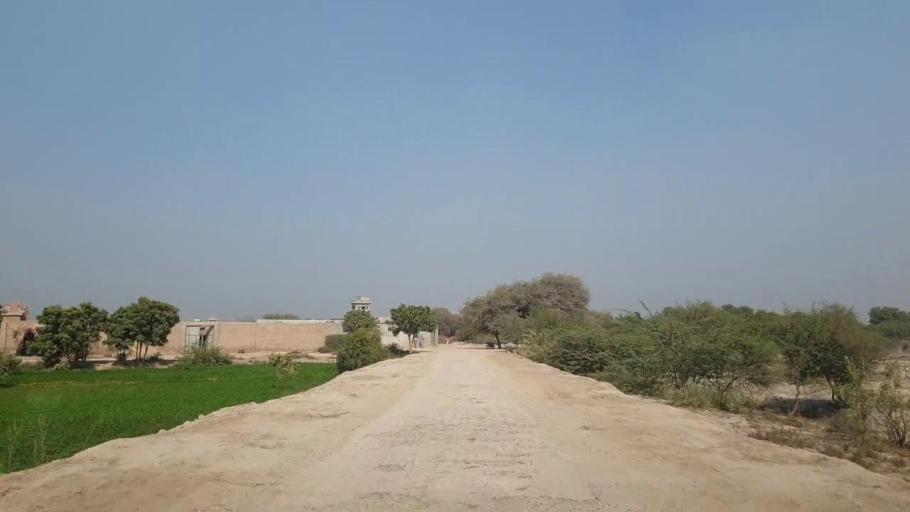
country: PK
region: Sindh
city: Tando Allahyar
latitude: 25.5044
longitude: 68.8349
